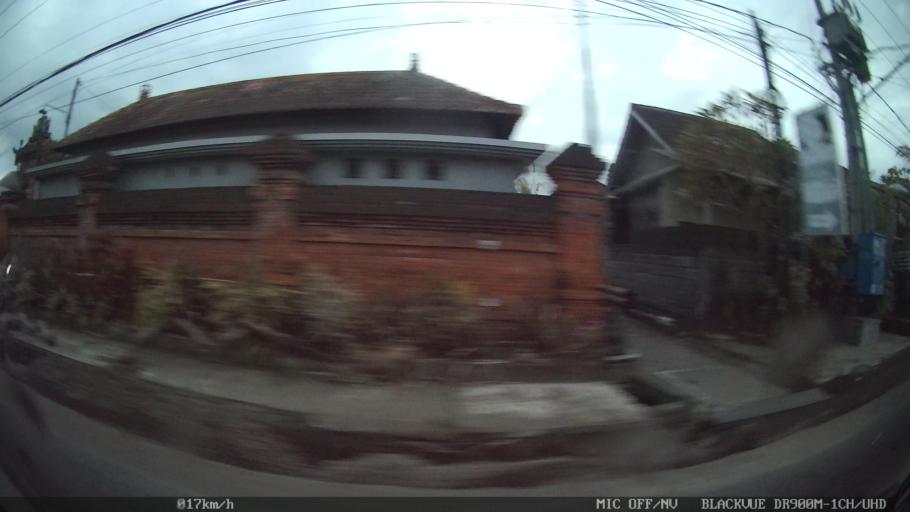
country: ID
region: Bali
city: Banjar Pasekan
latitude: -8.6389
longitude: 115.2737
